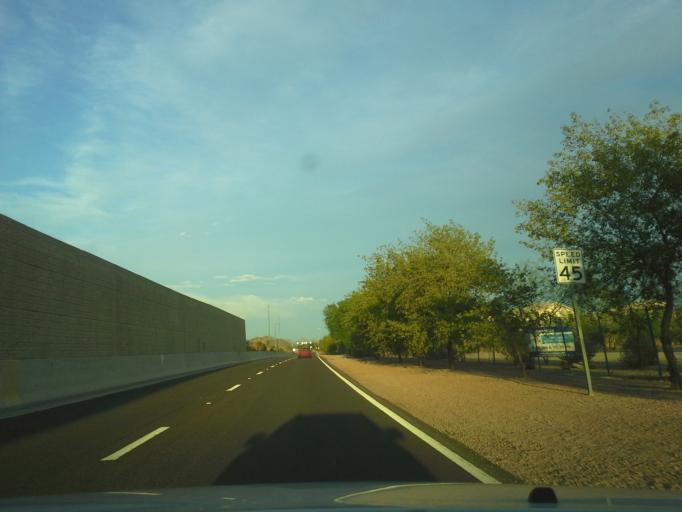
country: US
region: Arizona
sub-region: Maricopa County
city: Glendale
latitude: 33.6690
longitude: -112.0904
